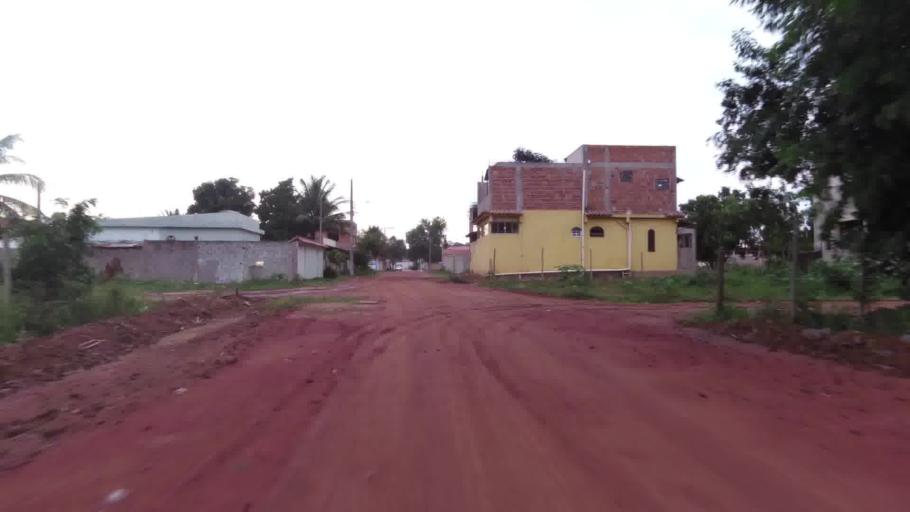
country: BR
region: Espirito Santo
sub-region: Piuma
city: Piuma
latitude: -20.8080
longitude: -40.6321
